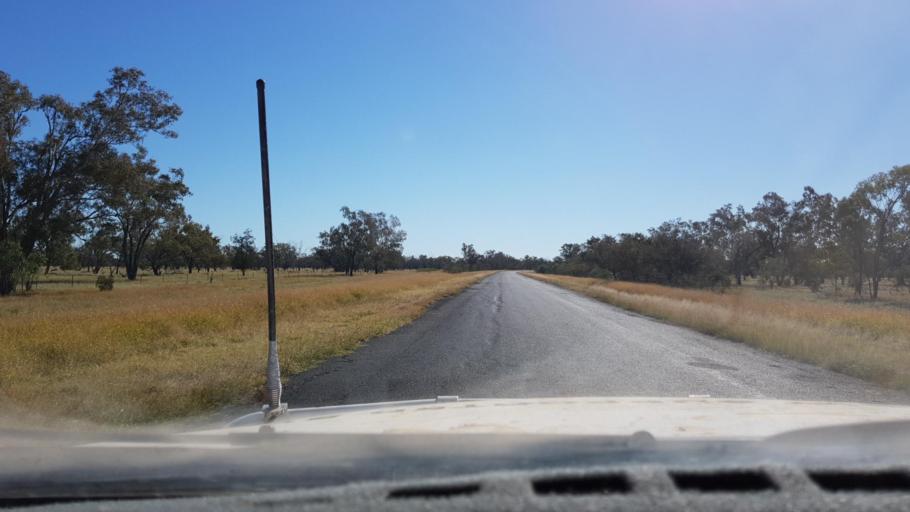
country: AU
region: New South Wales
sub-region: Walgett
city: Lightning Ridge
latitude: -29.5700
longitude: 148.6661
